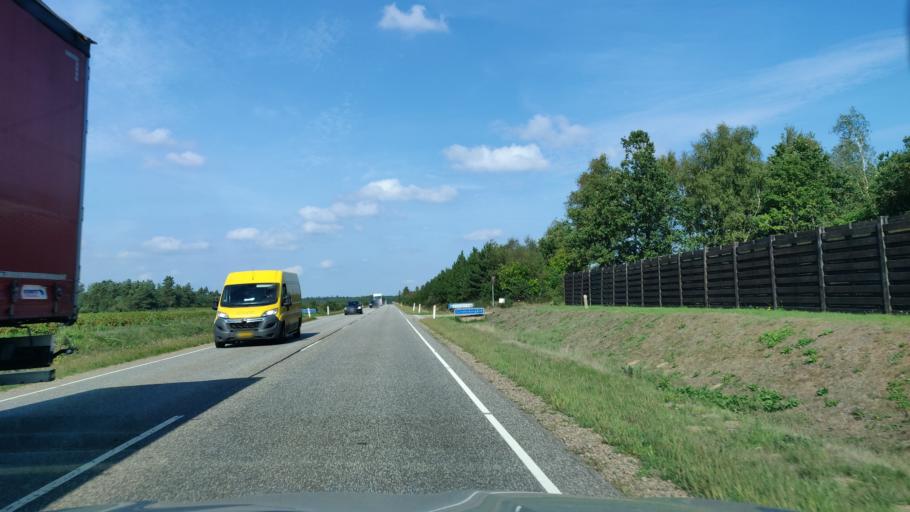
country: DK
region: Central Jutland
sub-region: Herning Kommune
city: Sunds
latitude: 56.3392
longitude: 8.9806
